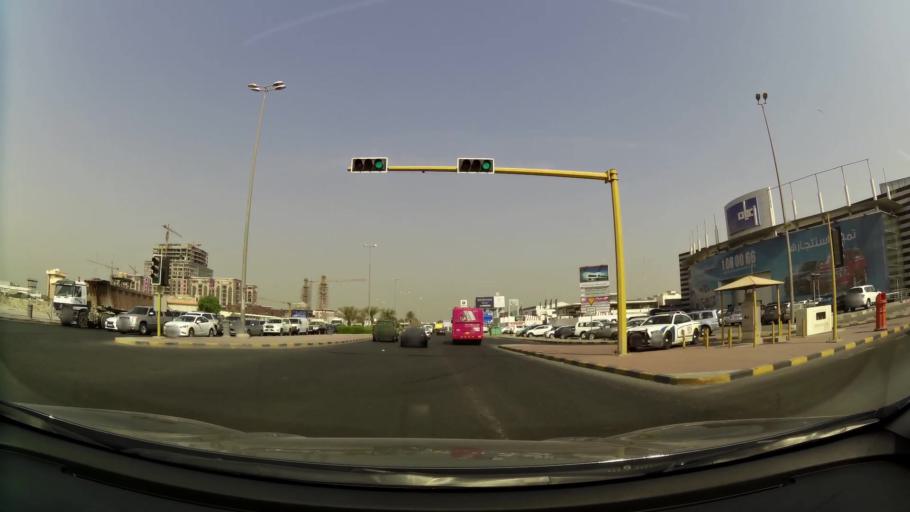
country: KW
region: Al Asimah
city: Ar Rabiyah
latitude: 29.3078
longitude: 47.9269
